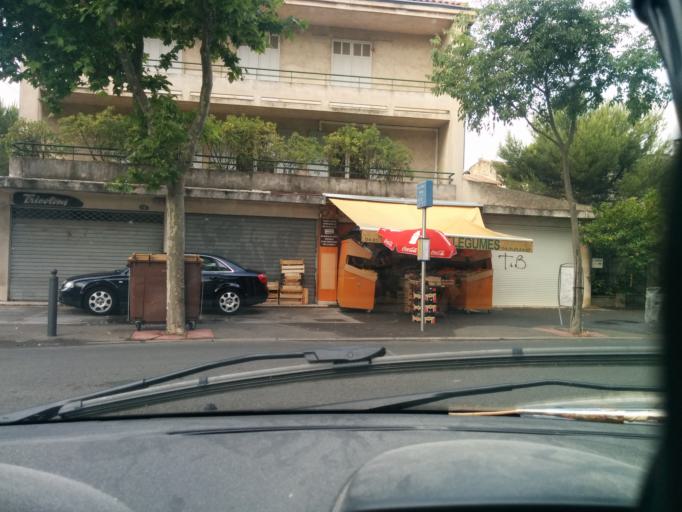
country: FR
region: Provence-Alpes-Cote d'Azur
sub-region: Departement des Bouches-du-Rhone
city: Plan-de-Cuques
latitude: 43.3241
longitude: 5.4561
